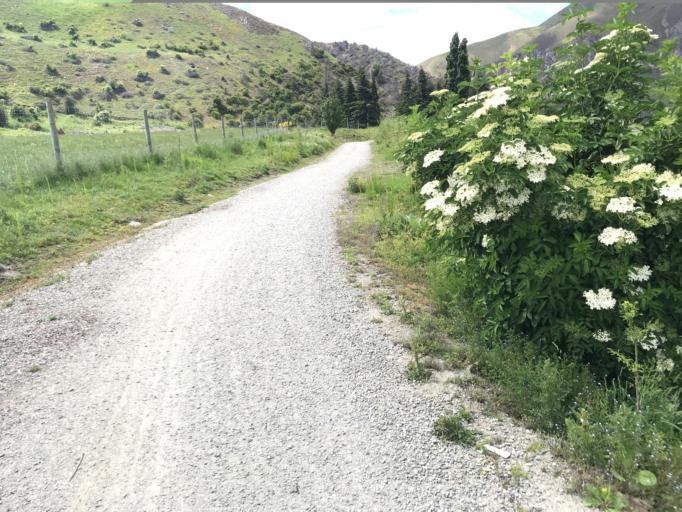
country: NZ
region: Otago
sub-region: Queenstown-Lakes District
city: Arrowtown
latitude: -45.0022
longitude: 168.8762
